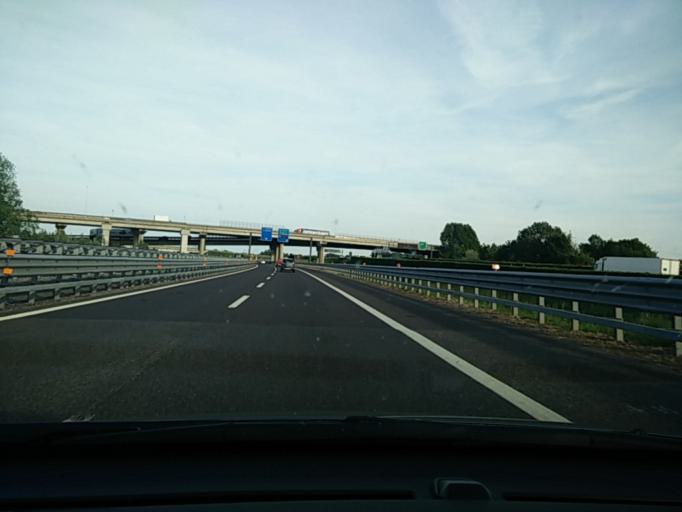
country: IT
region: Veneto
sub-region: Provincia di Padova
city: Cadoneghe
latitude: 45.4283
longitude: 11.9218
